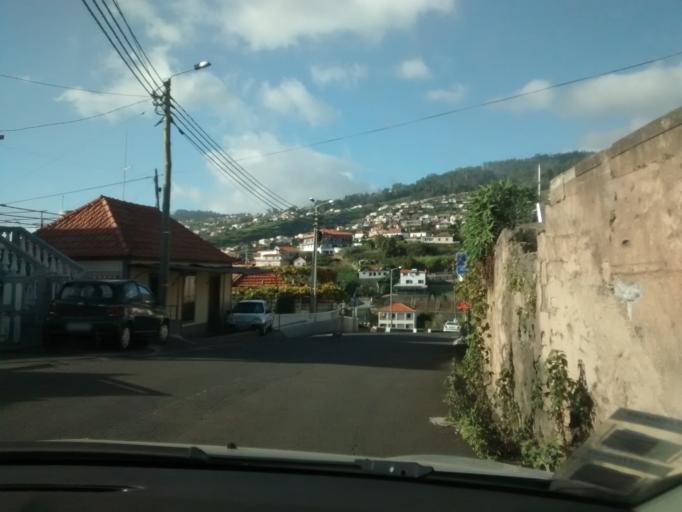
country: PT
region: Madeira
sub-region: Calheta
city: Estreito da Calheta
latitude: 32.7294
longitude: -17.1723
